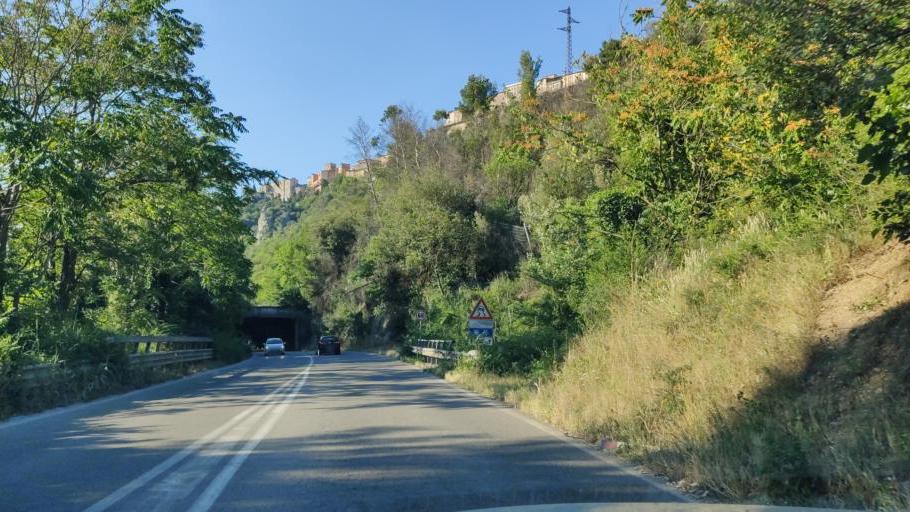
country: IT
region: Umbria
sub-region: Provincia di Terni
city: Narni
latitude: 42.5119
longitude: 12.5149
